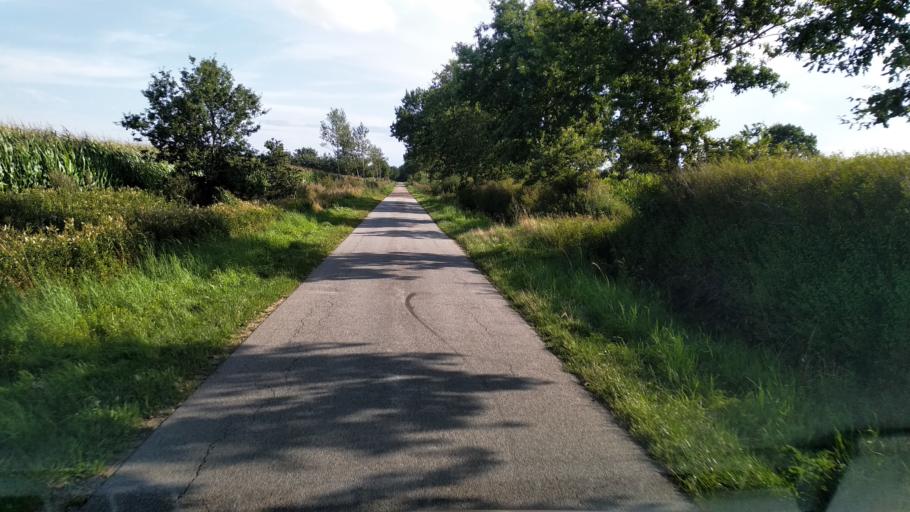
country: DE
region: Schleswig-Holstein
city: Gross Rheide
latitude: 54.4318
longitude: 9.4289
